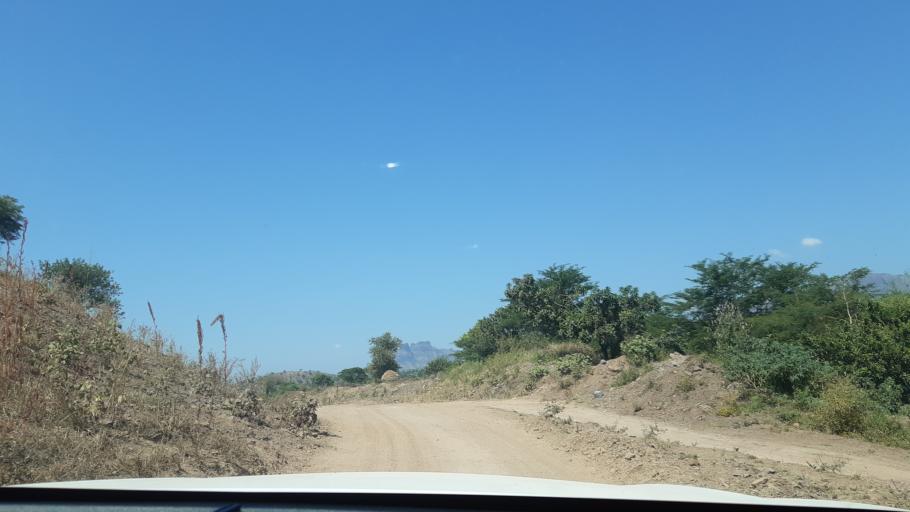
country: ET
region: Amhara
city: Dabat
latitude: 13.1932
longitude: 37.5663
